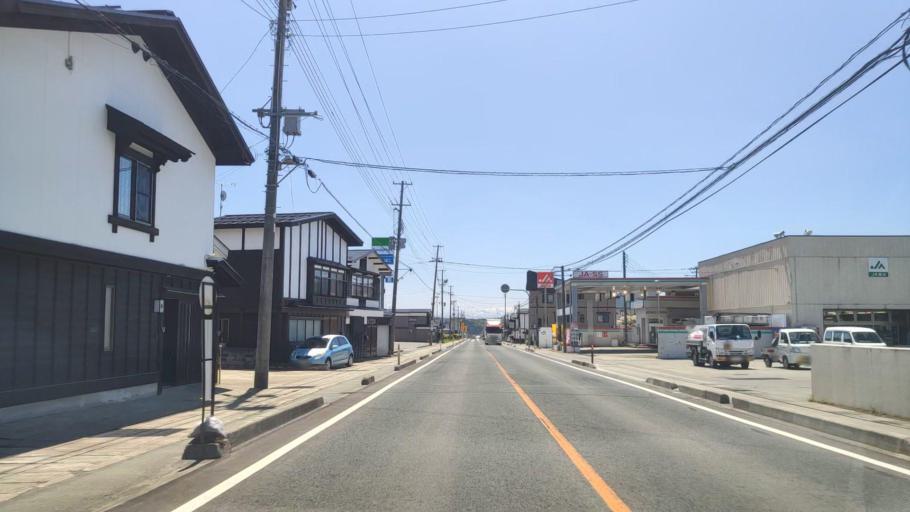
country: JP
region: Yamagata
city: Shinjo
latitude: 38.8806
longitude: 140.3363
